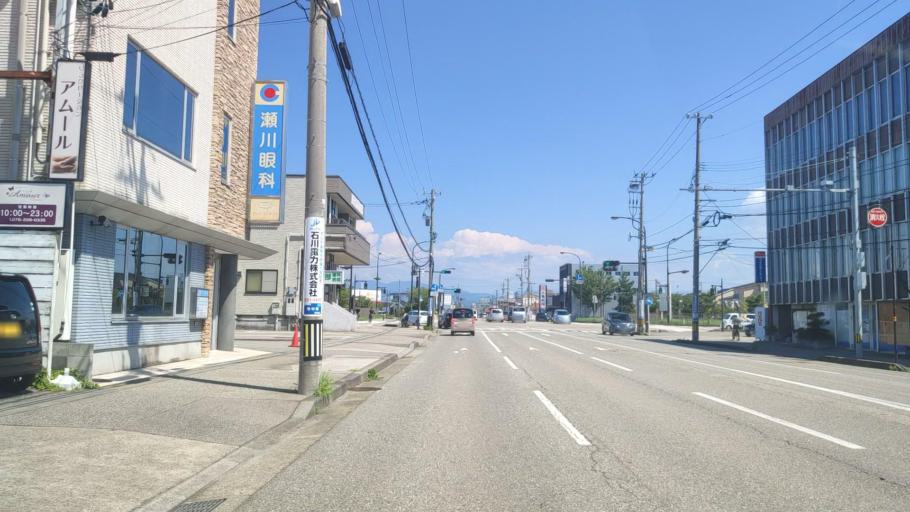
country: JP
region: Ishikawa
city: Kanazawa-shi
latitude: 36.5954
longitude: 136.6048
